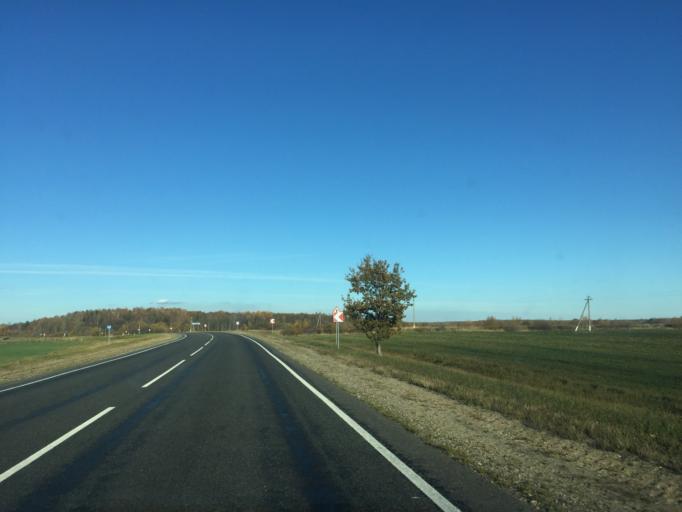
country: BY
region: Vitebsk
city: Dzisna
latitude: 55.3143
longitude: 28.2697
